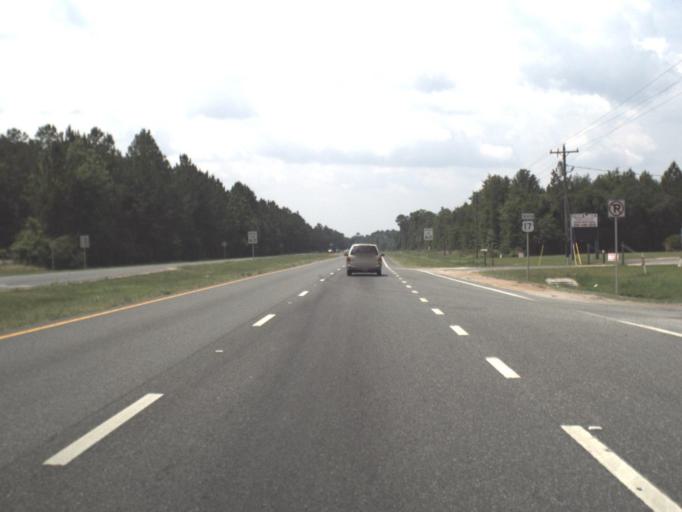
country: US
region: Florida
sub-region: Putnam County
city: Palatka
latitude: 29.7153
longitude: -81.6582
